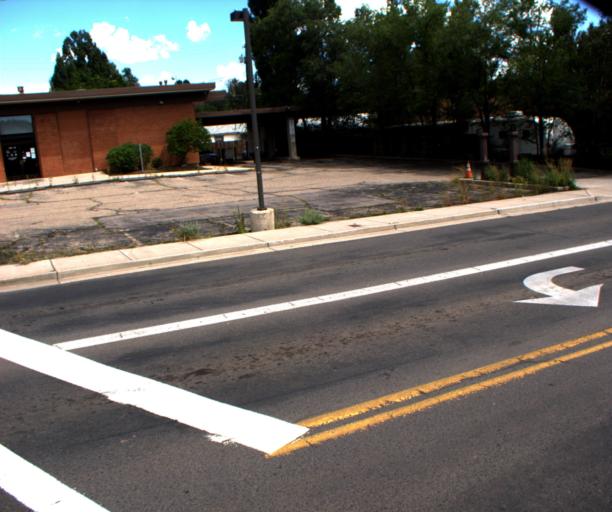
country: US
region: Arizona
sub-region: Coconino County
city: Flagstaff
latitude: 35.2065
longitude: -111.6476
